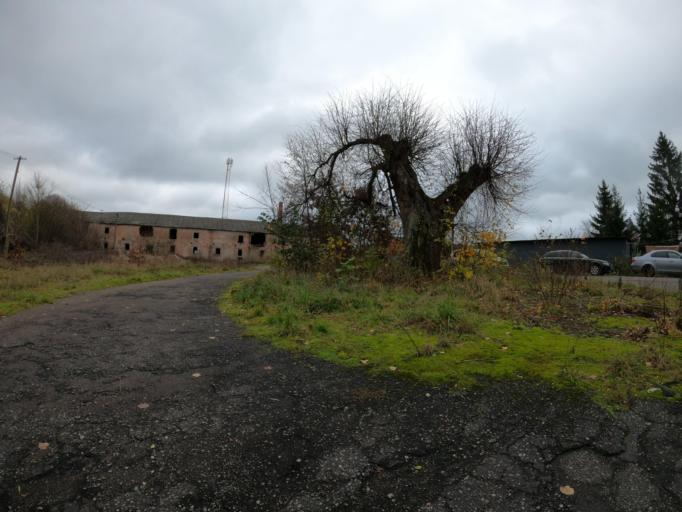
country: PL
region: West Pomeranian Voivodeship
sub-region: Powiat walecki
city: Tuczno
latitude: 53.2687
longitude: 16.1842
